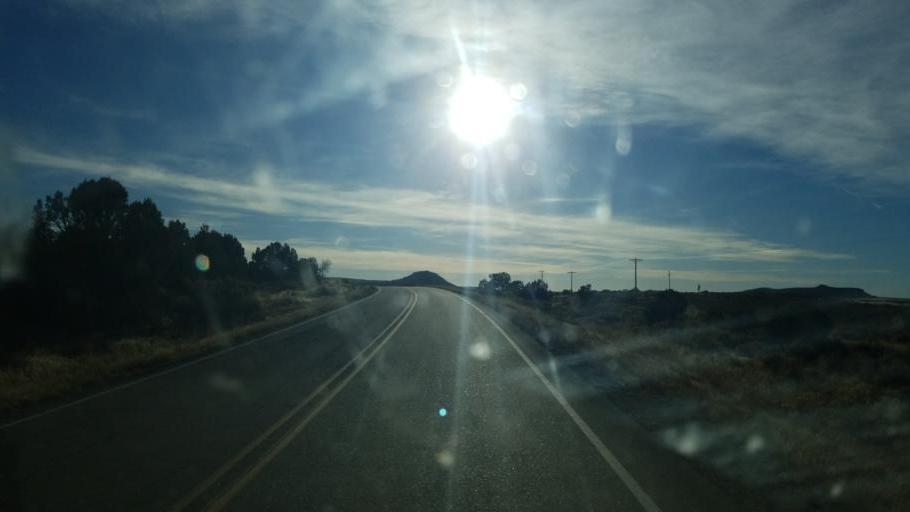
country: US
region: New Mexico
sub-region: San Juan County
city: Bloomfield
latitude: 36.7521
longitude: -107.6132
